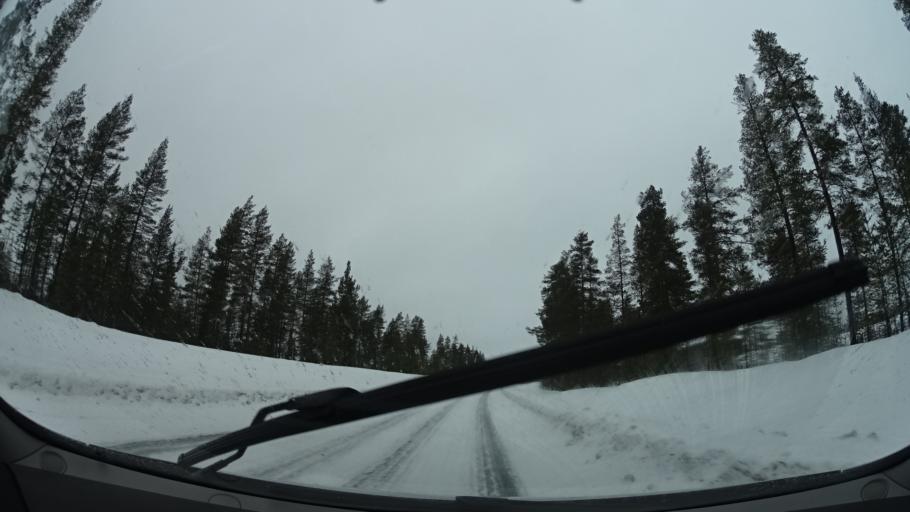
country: SE
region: Vaesterbotten
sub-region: Mala Kommun
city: Mala
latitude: 65.1428
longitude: 18.8353
